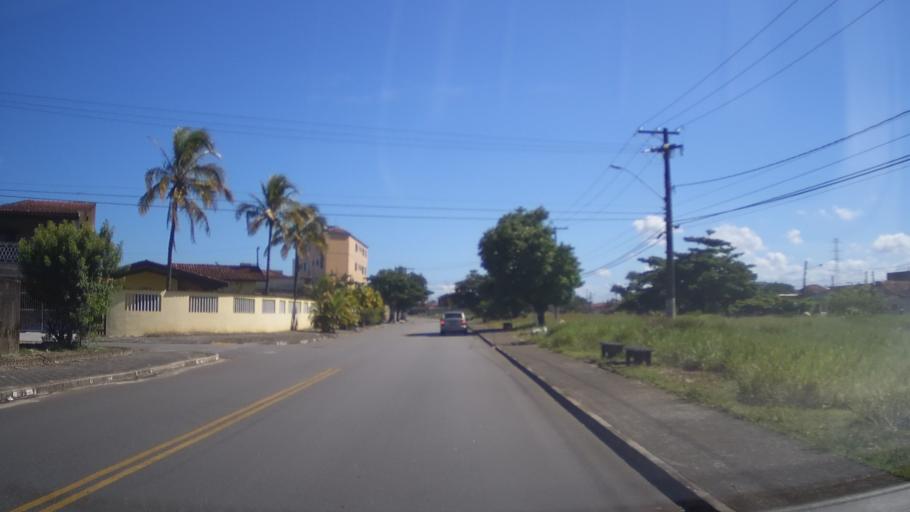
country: BR
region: Sao Paulo
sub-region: Mongagua
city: Mongagua
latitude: -24.1224
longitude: -46.6752
